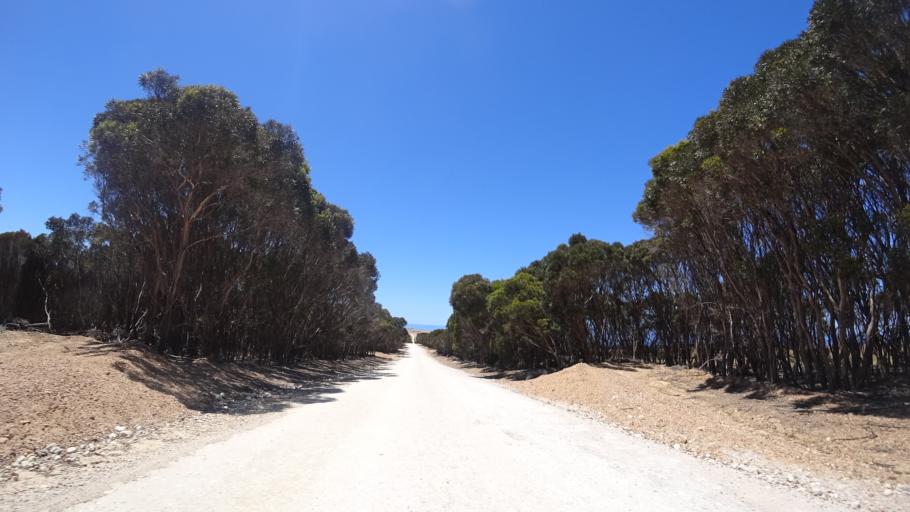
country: AU
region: South Australia
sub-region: Yankalilla
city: Normanville
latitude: -35.8356
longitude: 138.1084
